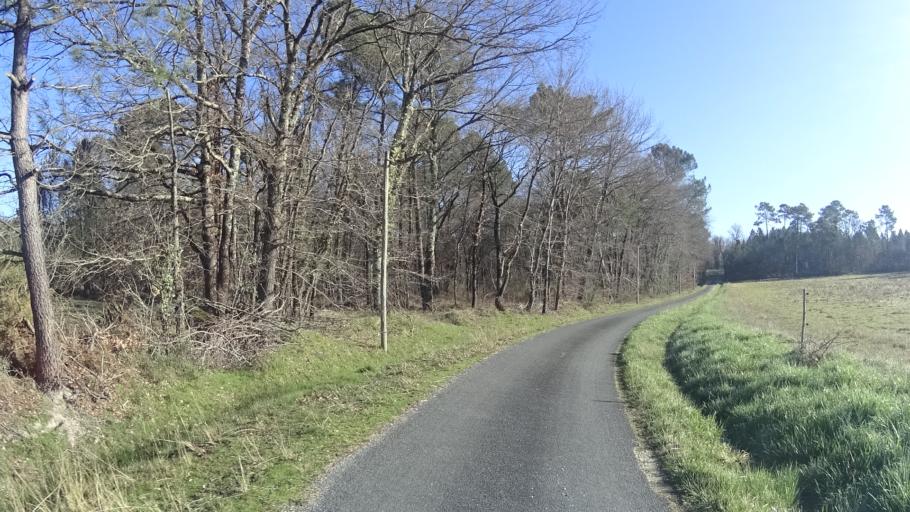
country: FR
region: Aquitaine
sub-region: Departement de la Dordogne
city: La Roche-Chalais
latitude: 45.1596
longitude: 0.0213
